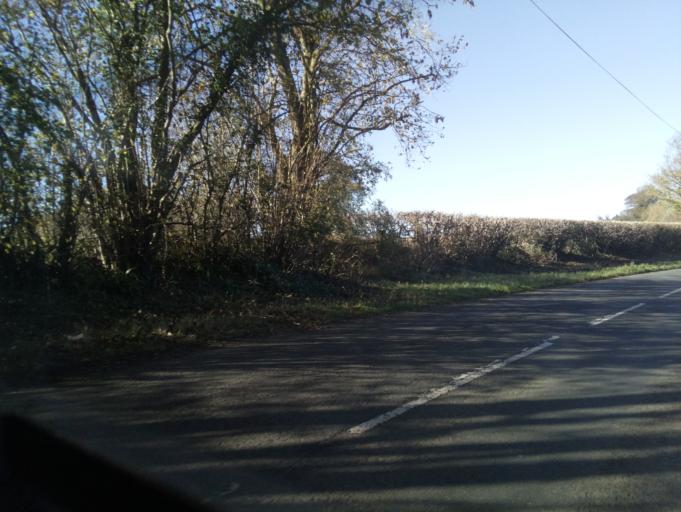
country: GB
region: England
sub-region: Somerset
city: Yeovil
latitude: 50.9590
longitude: -2.6576
